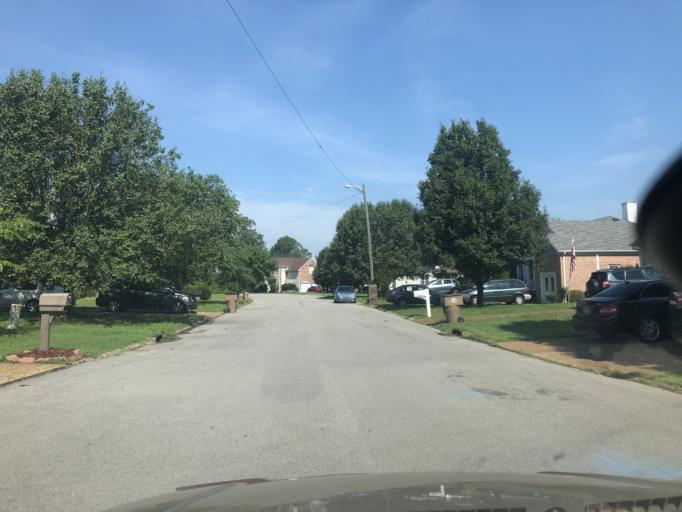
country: US
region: Tennessee
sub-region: Davidson County
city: Lakewood
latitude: 36.2397
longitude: -86.6988
